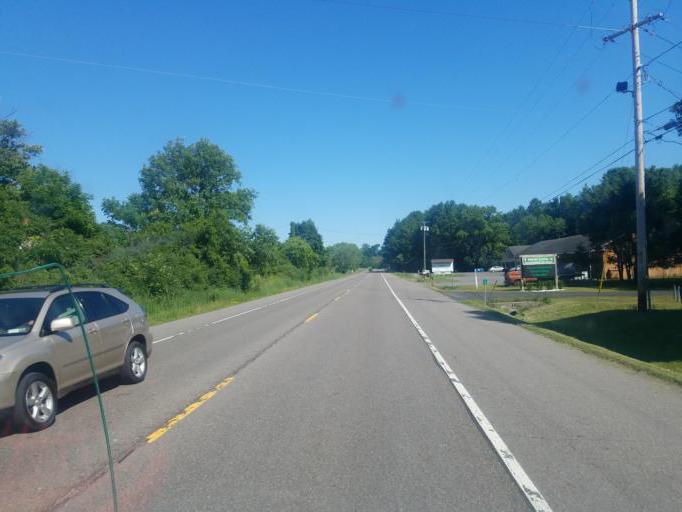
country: US
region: New York
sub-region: Wayne County
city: Lyons
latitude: 43.0623
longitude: -77.0208
